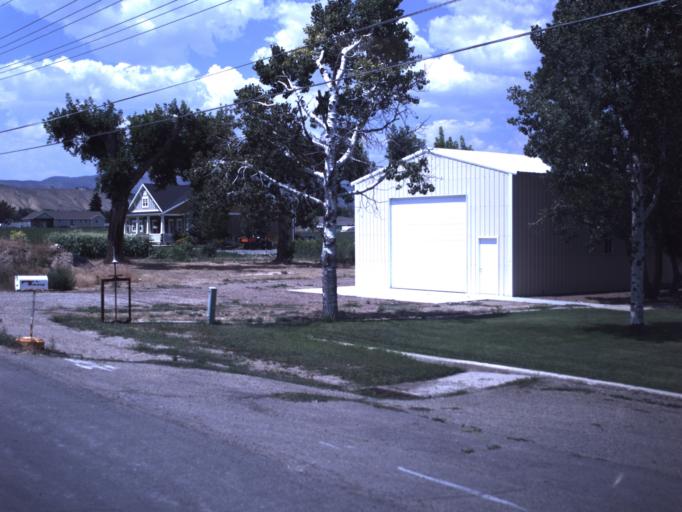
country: US
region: Utah
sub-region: Uintah County
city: Maeser
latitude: 40.4627
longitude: -109.5822
